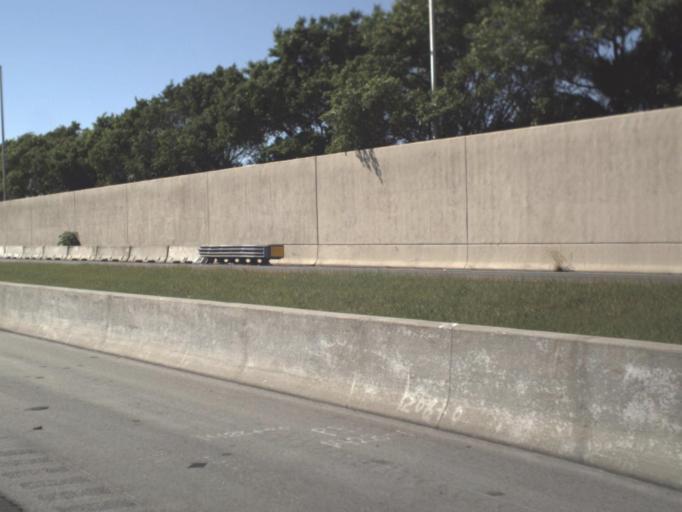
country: US
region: Florida
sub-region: Miami-Dade County
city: Three Lakes
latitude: 25.6446
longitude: -80.3860
